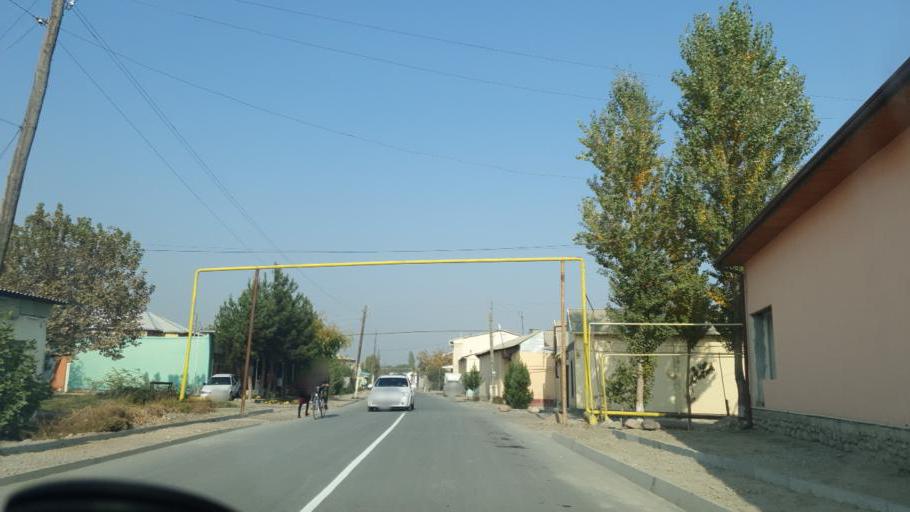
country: UZ
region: Fergana
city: Qo`qon
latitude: 40.5820
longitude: 70.9110
